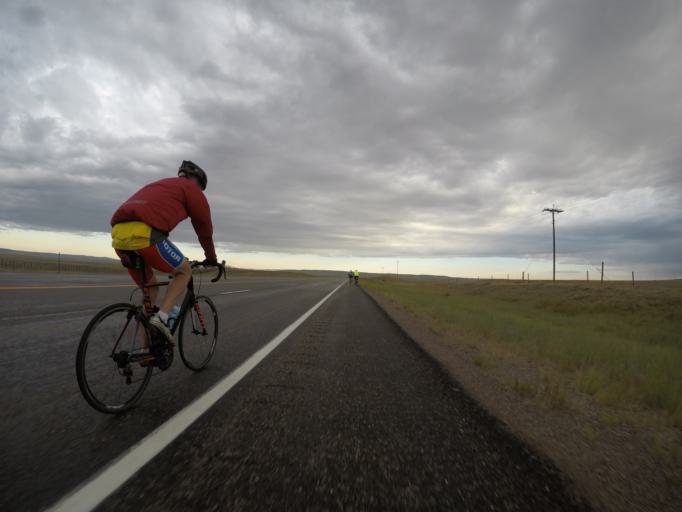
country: US
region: Wyoming
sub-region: Albany County
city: Laramie
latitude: 41.8314
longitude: -106.0154
